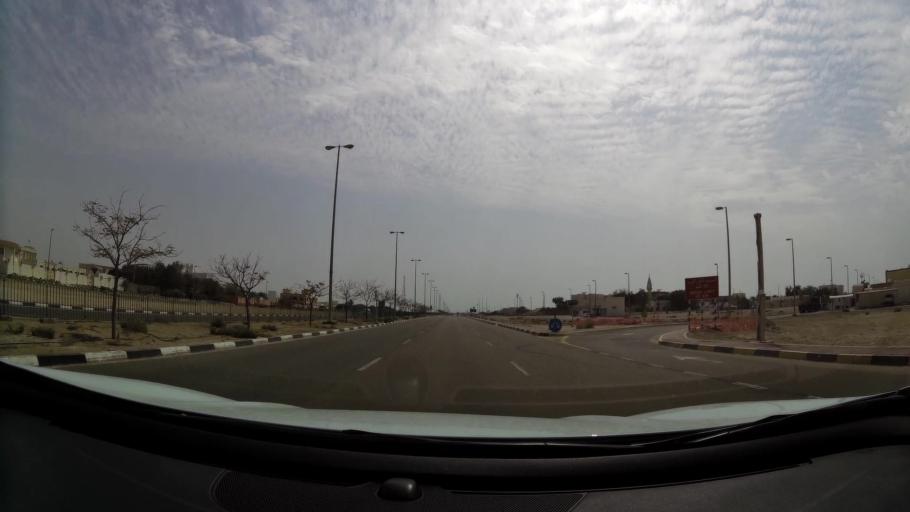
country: AE
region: Abu Dhabi
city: Abu Dhabi
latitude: 24.5582
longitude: 54.6857
